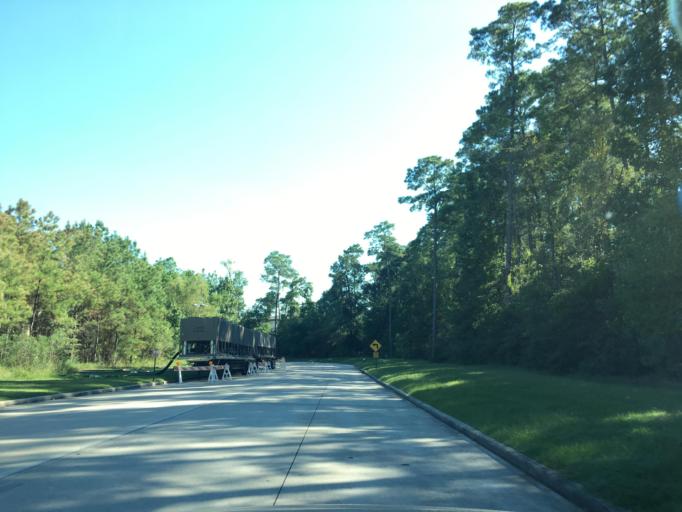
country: US
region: Texas
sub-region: Montgomery County
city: Shenandoah
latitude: 30.2008
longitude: -95.4595
